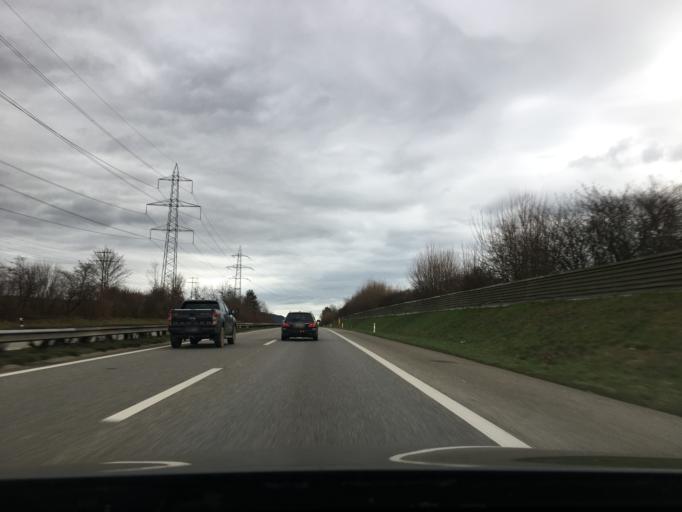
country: CH
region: Aargau
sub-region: Bezirk Rheinfelden
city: Mohlin
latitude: 47.5477
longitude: 7.8724
